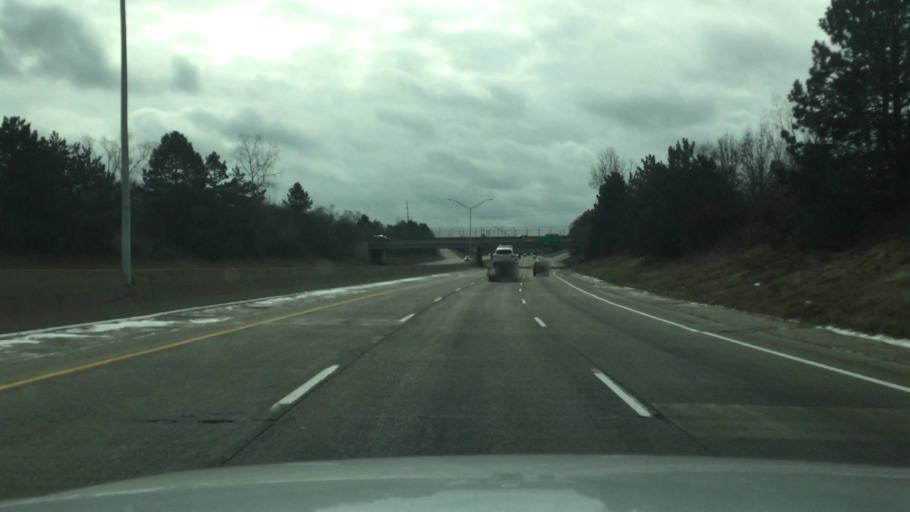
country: US
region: Michigan
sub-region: Genesee County
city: Beecher
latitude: 43.0776
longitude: -83.6838
